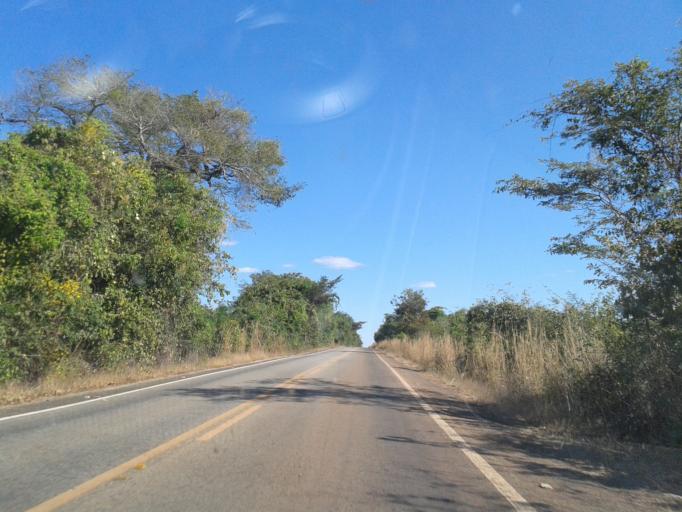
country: BR
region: Goias
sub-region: Mozarlandia
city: Mozarlandia
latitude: -14.4342
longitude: -50.4560
